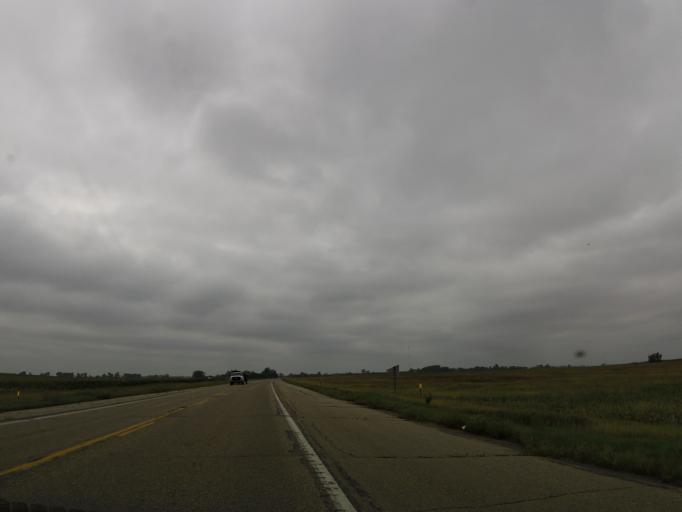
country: US
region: South Dakota
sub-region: Deuel County
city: Clear Lake
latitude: 44.9332
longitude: -96.6442
